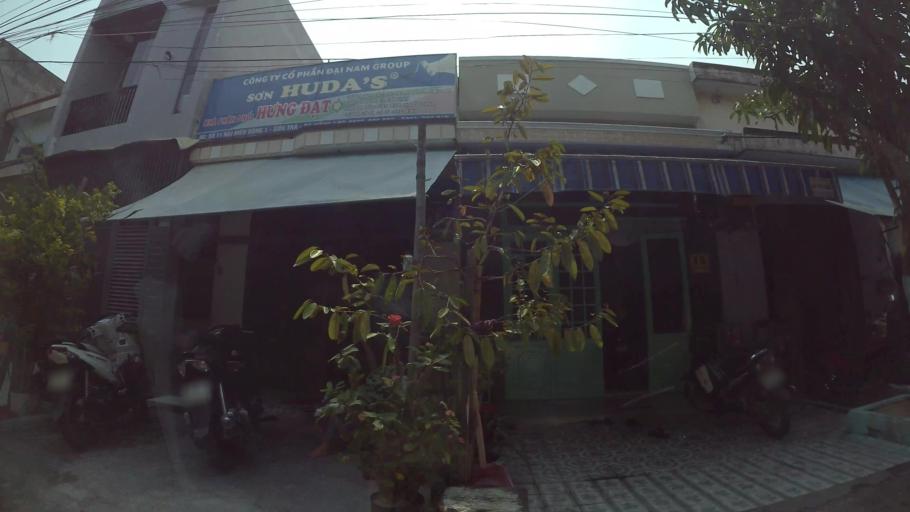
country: VN
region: Da Nang
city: Da Nang
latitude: 16.0920
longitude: 108.2358
